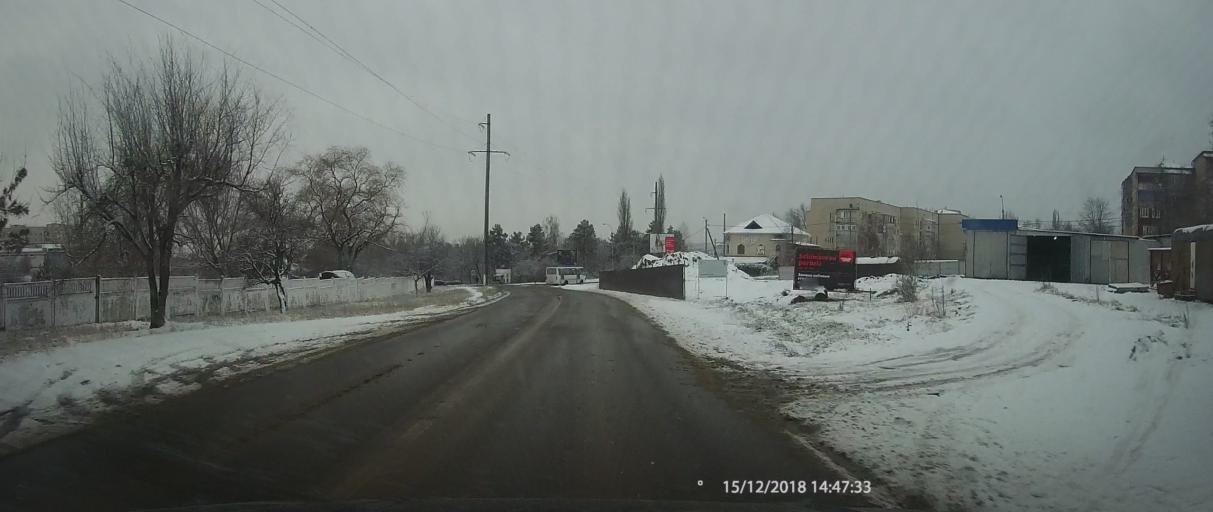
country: MD
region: Cahul
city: Cahul
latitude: 45.8948
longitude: 28.2052
